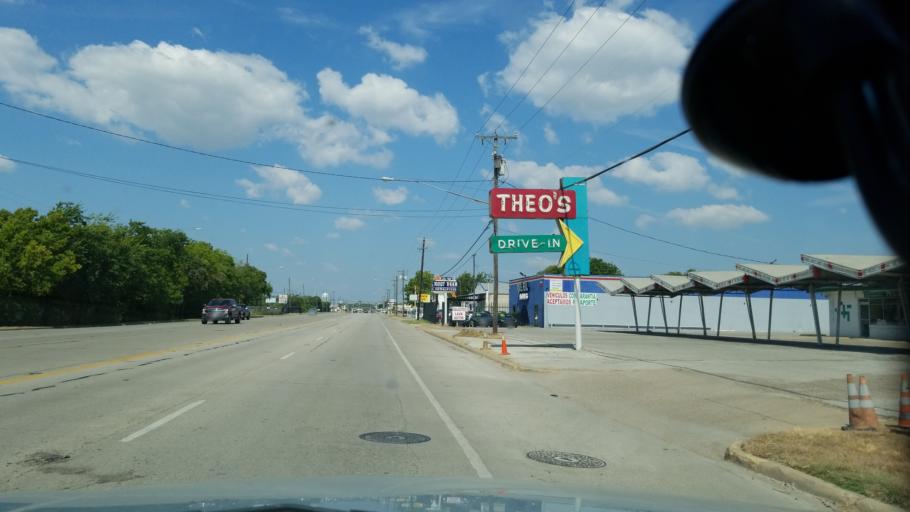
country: US
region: Texas
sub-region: Dallas County
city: Grand Prairie
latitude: 32.7494
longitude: -96.9663
